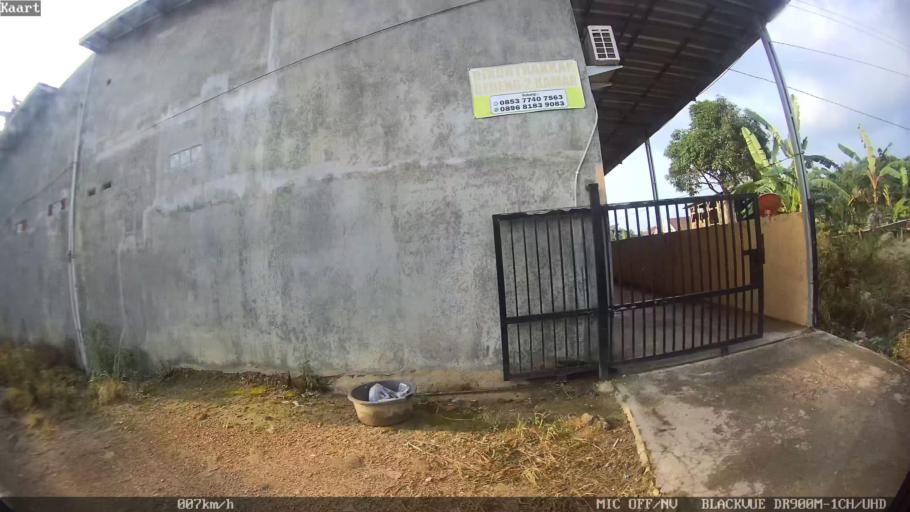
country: ID
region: Lampung
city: Kedaton
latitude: -5.3919
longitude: 105.3240
